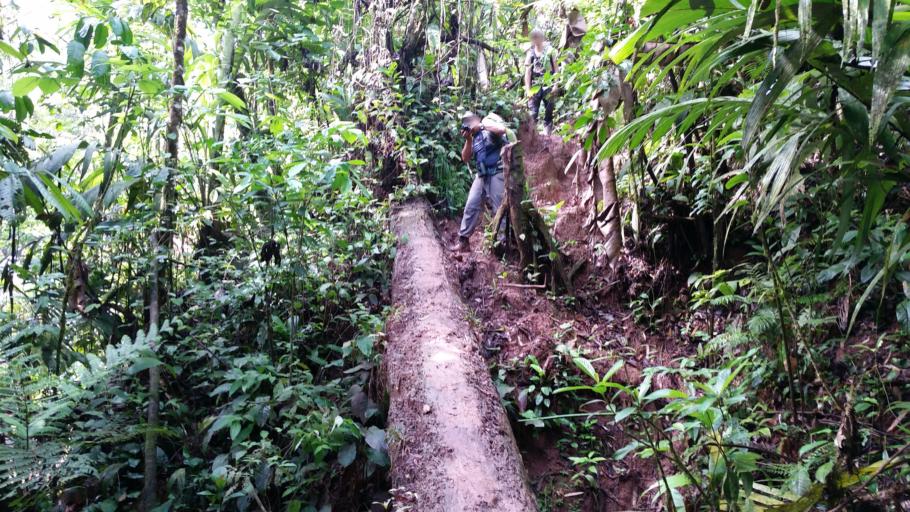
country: NI
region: Atlantico Norte (RAAN)
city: Bonanza
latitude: 14.0888
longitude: -84.6887
